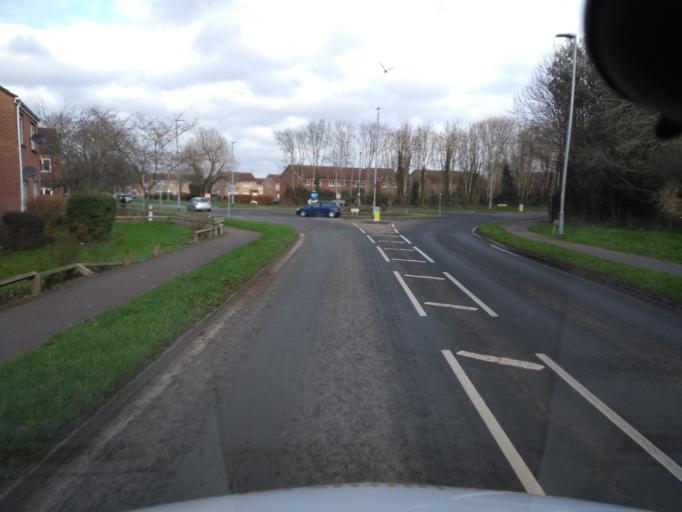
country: GB
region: England
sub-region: Somerset
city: Taunton
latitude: 51.0092
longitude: -3.0750
